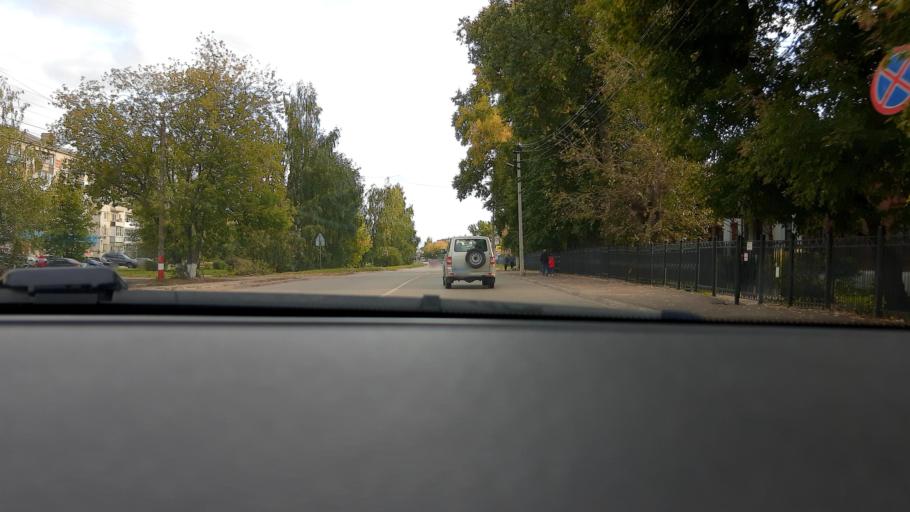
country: RU
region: Nizjnij Novgorod
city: Novaya Balakhna
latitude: 56.5028
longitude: 43.6029
